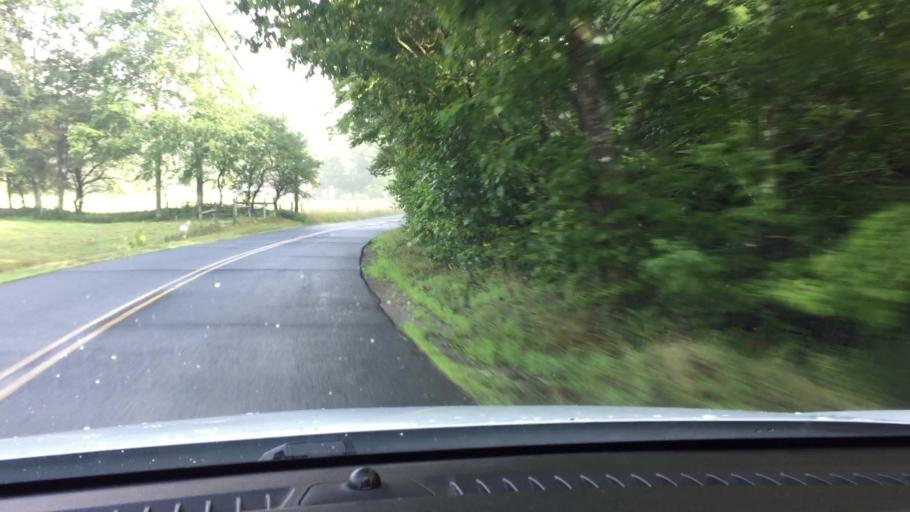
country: US
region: Massachusetts
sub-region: Berkshire County
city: Becket
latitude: 42.3952
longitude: -72.9791
